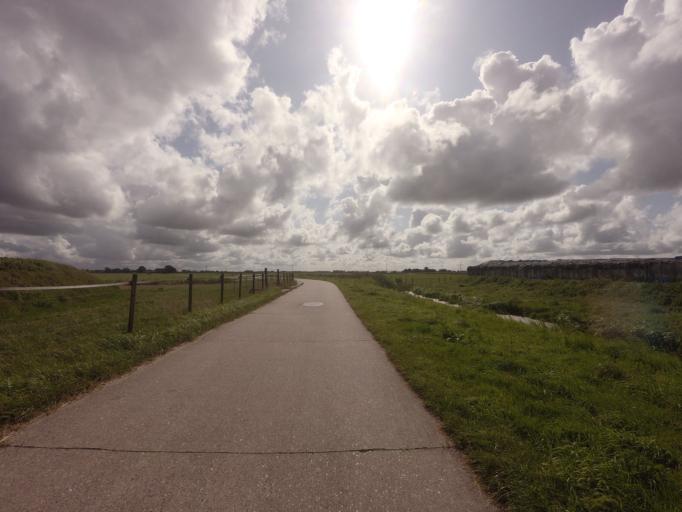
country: NL
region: Friesland
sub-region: Sudwest Fryslan
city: Scharnegoutum
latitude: 53.0711
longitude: 5.6373
